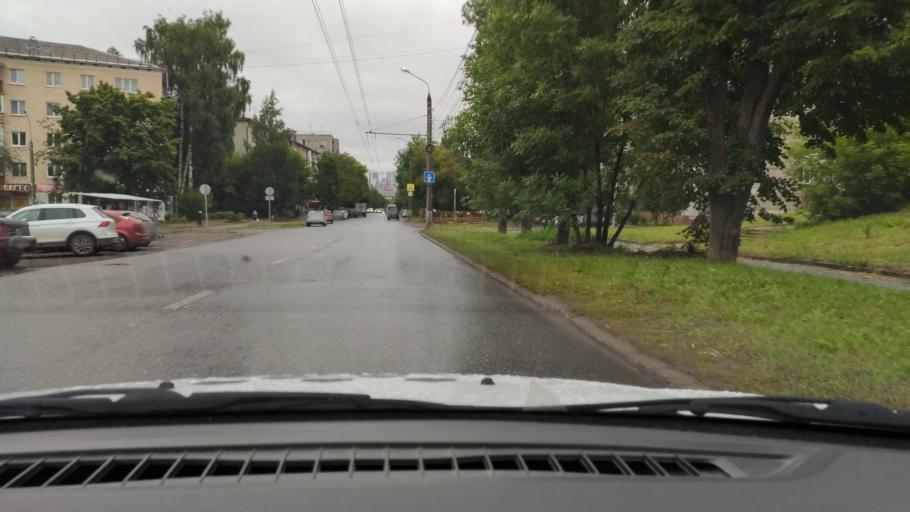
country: RU
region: Udmurtiya
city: Izhevsk
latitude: 56.8764
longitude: 53.1856
